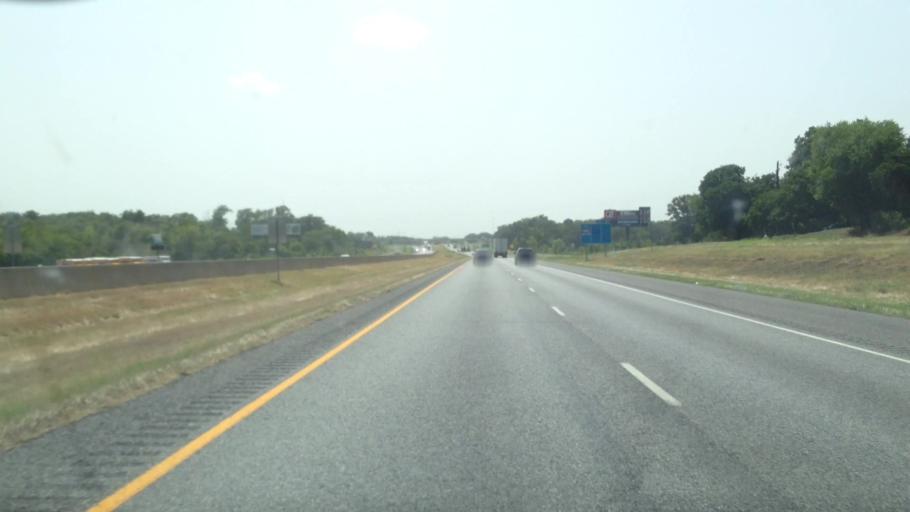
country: US
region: Texas
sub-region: Hunt County
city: Greenville
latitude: 33.1335
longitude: -96.0430
